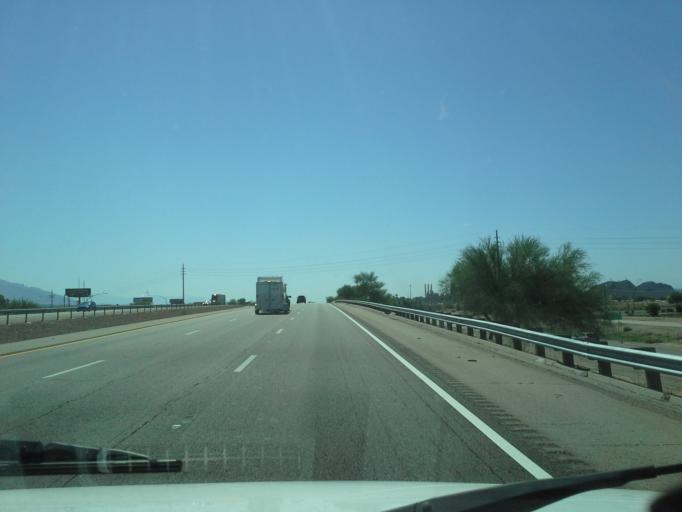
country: US
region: Arizona
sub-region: Pima County
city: Marana
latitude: 32.4258
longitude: -111.1659
